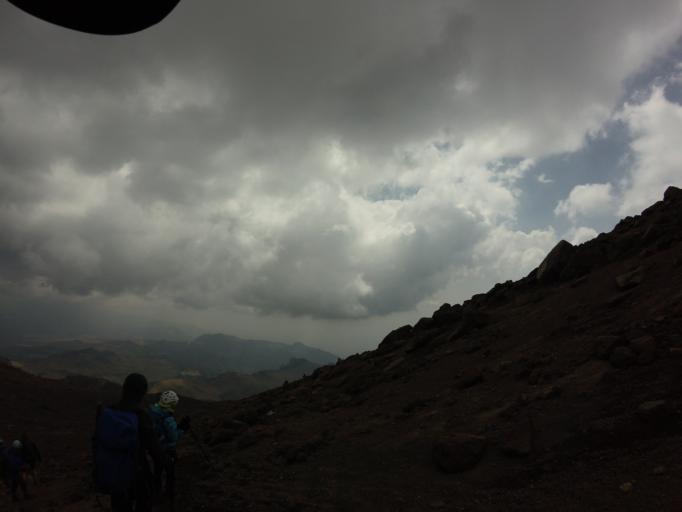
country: MX
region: Mexico
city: Amecameca de Juarez
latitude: 19.1649
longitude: -98.6457
